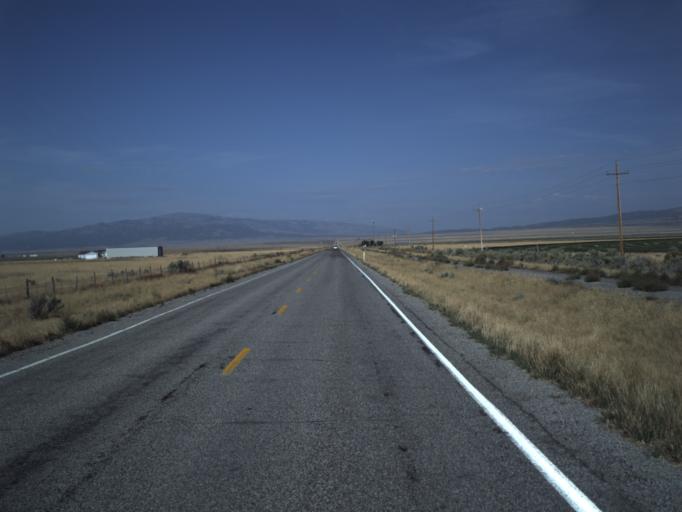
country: US
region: Idaho
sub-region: Oneida County
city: Malad City
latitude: 41.9666
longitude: -112.9055
